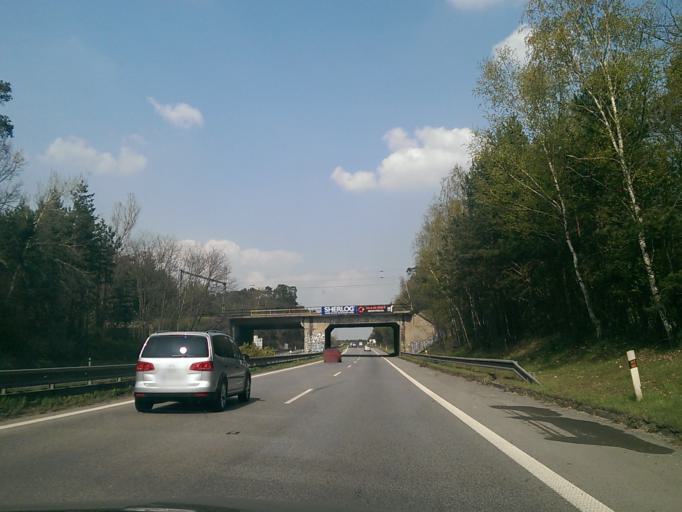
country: CZ
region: Central Bohemia
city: Brandys nad Labem-Stara Boleslav
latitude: 50.2064
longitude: 14.6956
